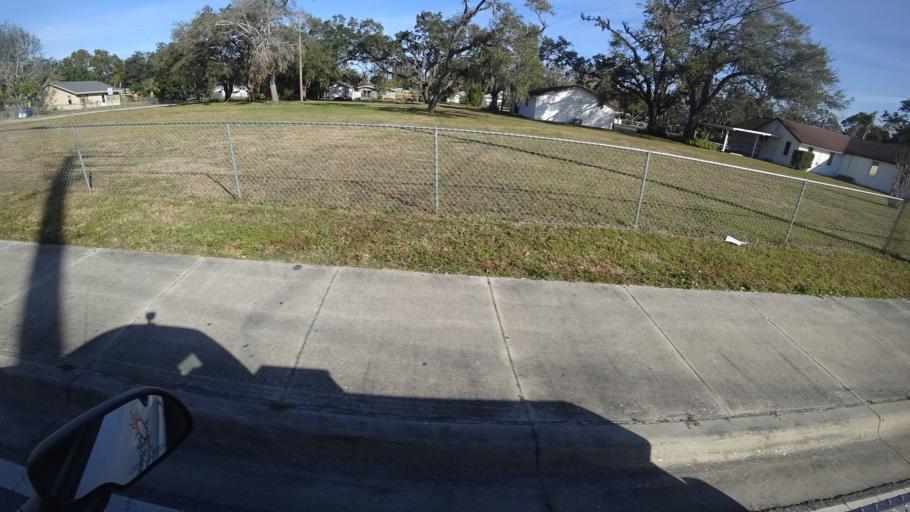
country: US
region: Florida
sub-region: Manatee County
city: West Samoset
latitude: 27.4771
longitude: -82.5584
